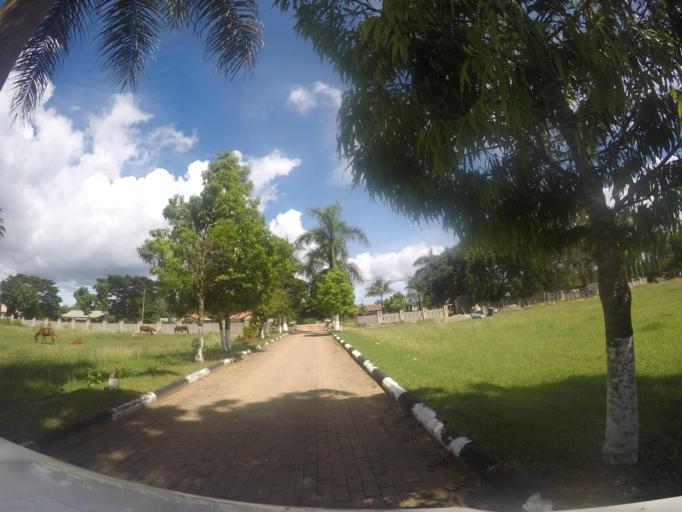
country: TL
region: Lautem
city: Lospalos
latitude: -8.4946
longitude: 126.9918
